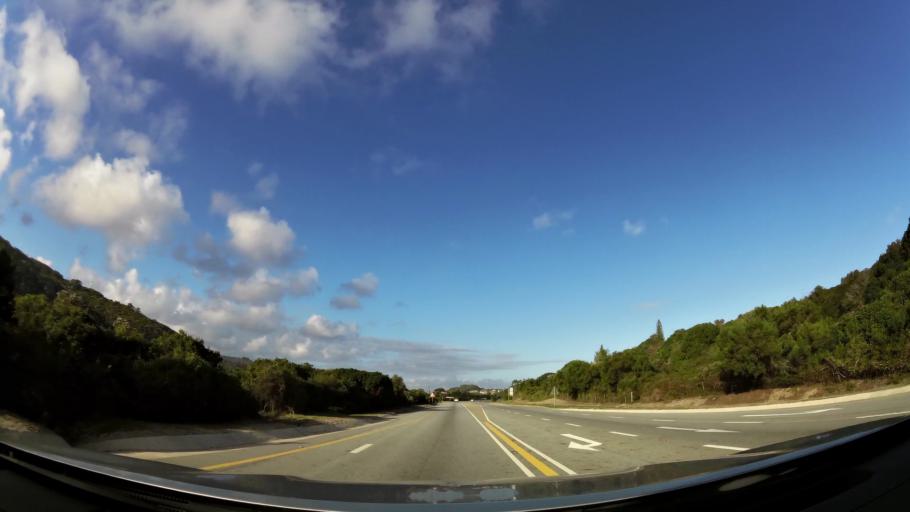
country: ZA
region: Western Cape
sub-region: Eden District Municipality
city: George
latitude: -33.9951
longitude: 22.5905
